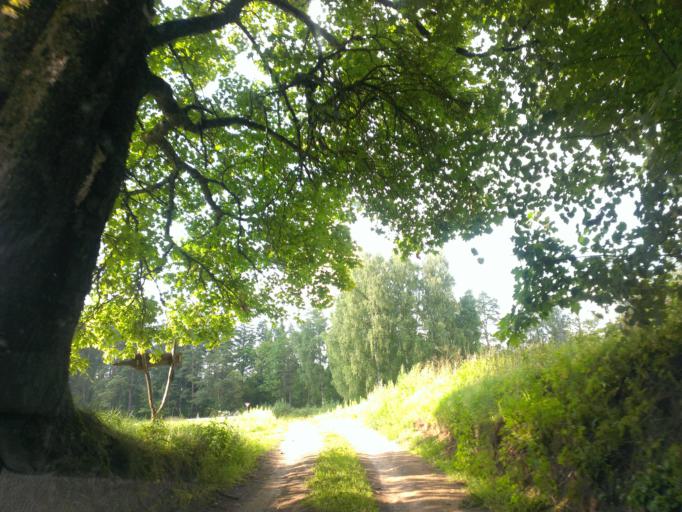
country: LV
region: Priekuli
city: Priekuli
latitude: 57.2926
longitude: 25.4739
